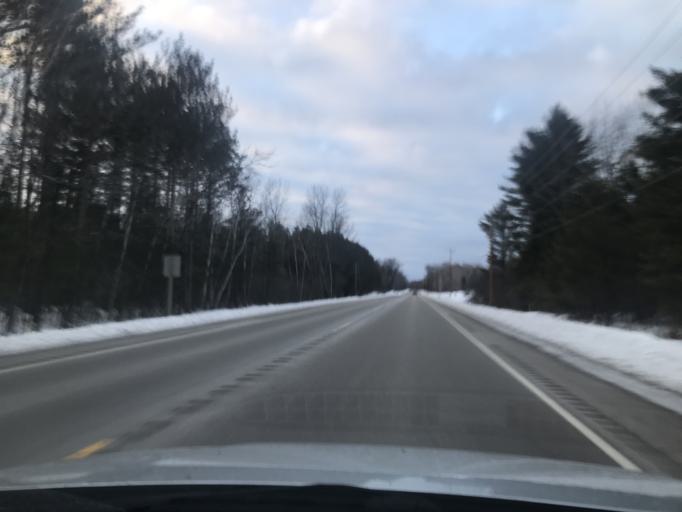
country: US
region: Wisconsin
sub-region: Marinette County
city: Marinette
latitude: 45.1473
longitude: -87.7002
